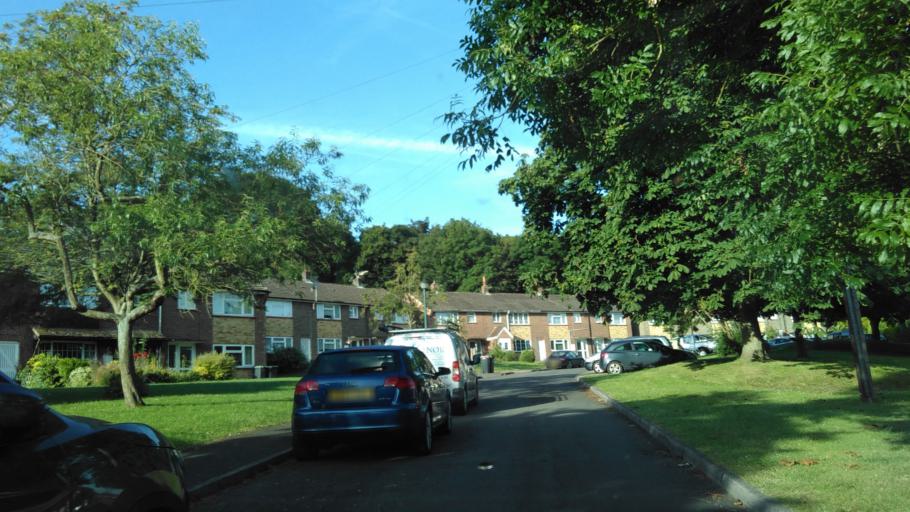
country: GB
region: England
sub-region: Kent
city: Chartham
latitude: 51.2531
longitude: 1.0175
